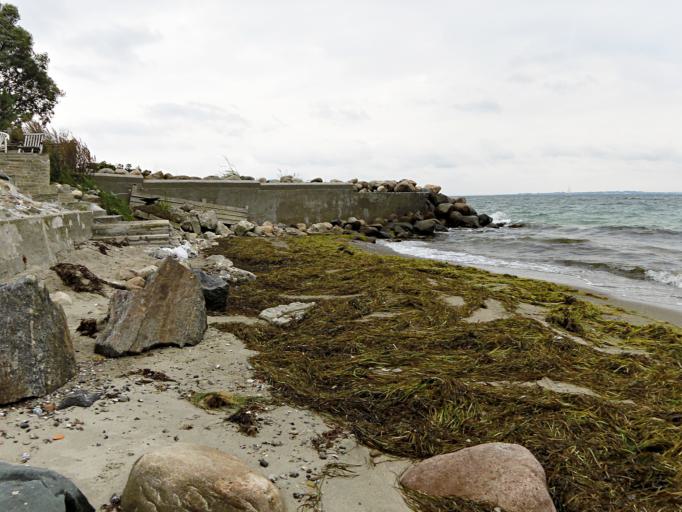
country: DK
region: Capital Region
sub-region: Rudersdal Kommune
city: Trorod
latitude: 55.8540
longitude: 12.5683
